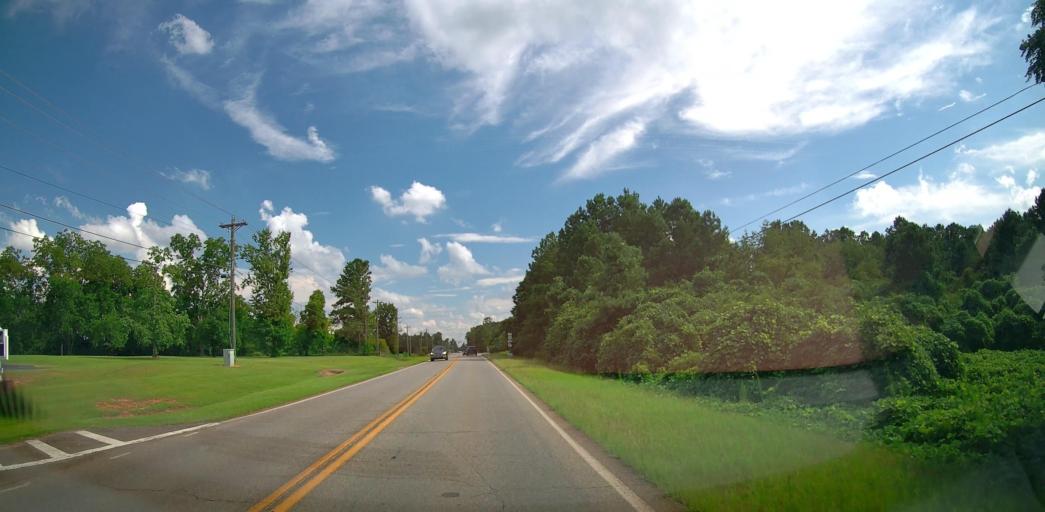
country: US
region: Georgia
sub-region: Houston County
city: Perry
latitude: 32.4897
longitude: -83.7300
